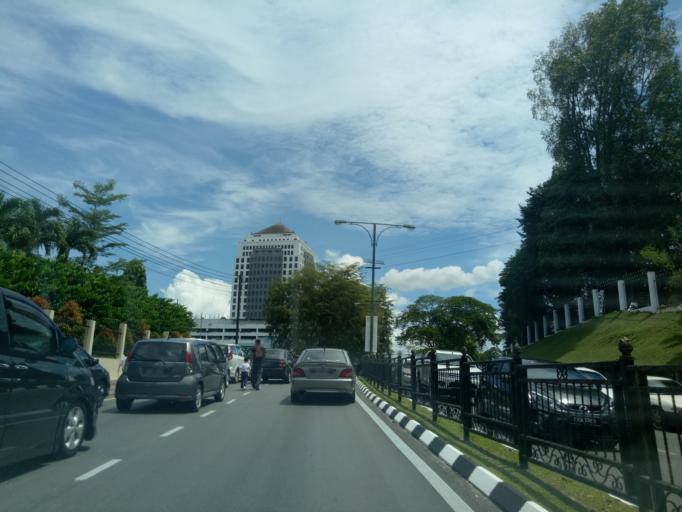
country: MY
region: Sarawak
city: Kuching
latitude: 1.5557
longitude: 110.3463
